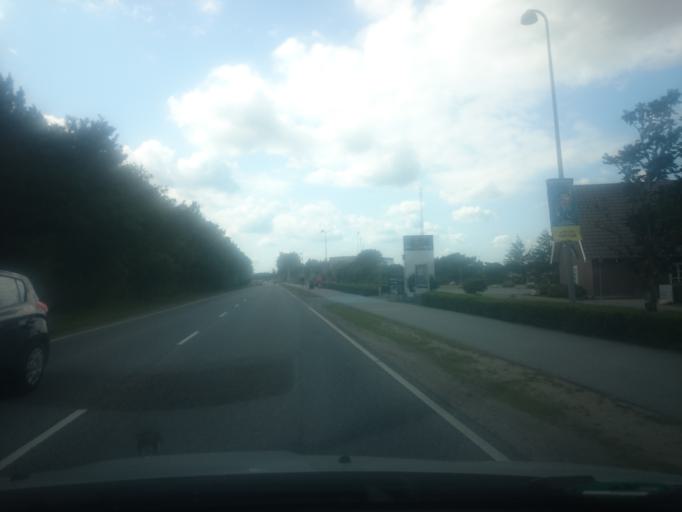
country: DK
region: South Denmark
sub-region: Billund Kommune
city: Billund
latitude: 55.7312
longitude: 9.1332
